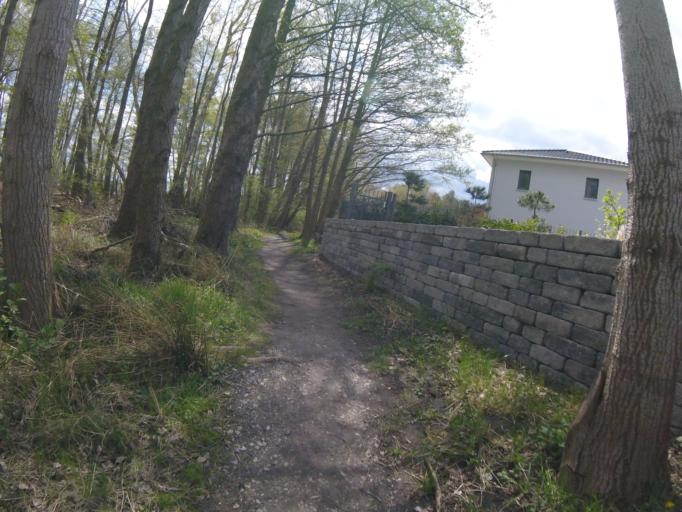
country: DE
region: Brandenburg
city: Bestensee
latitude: 52.2356
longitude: 13.6435
